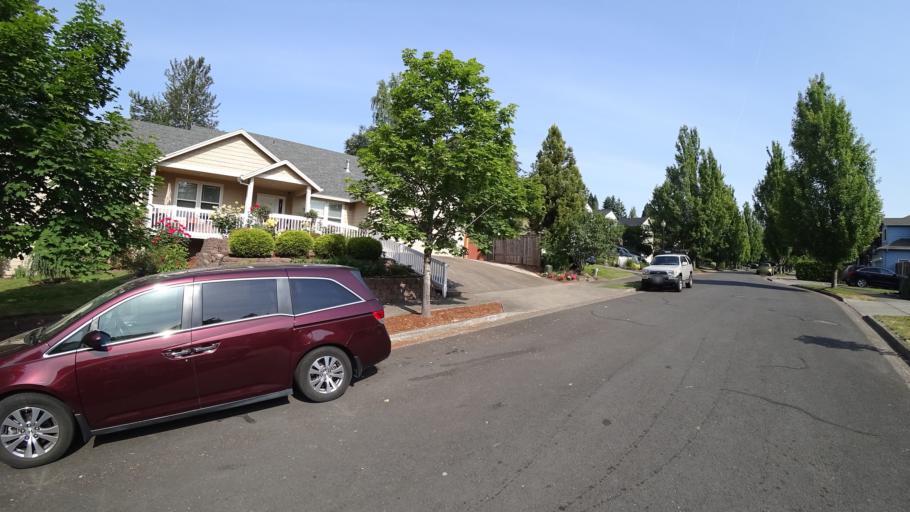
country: US
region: Oregon
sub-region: Clackamas County
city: Happy Valley
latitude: 45.4494
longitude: -122.5249
